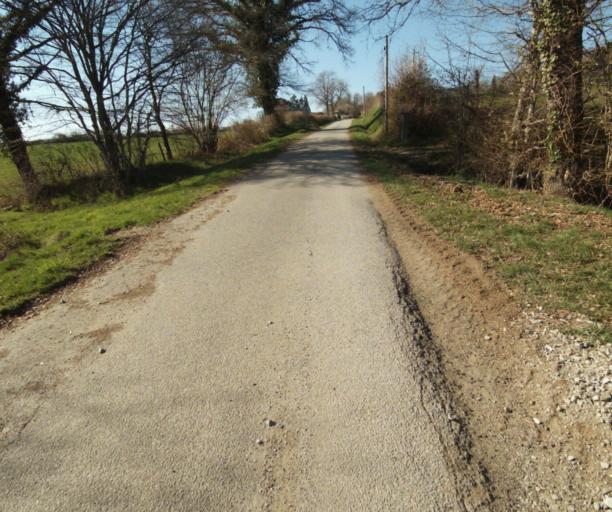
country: FR
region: Limousin
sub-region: Departement de la Correze
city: Chamboulive
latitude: 45.4779
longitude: 1.6909
